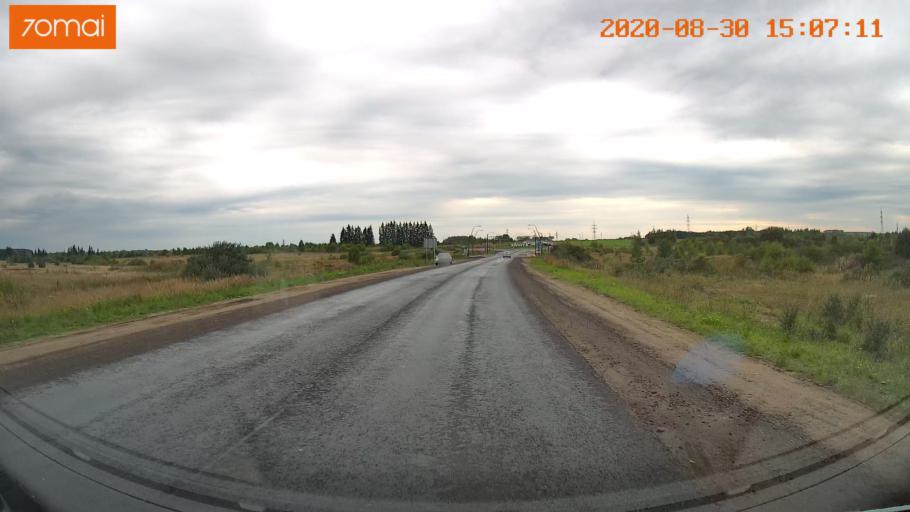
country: RU
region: Ivanovo
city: Staraya Vichuga
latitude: 57.2491
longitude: 41.8982
